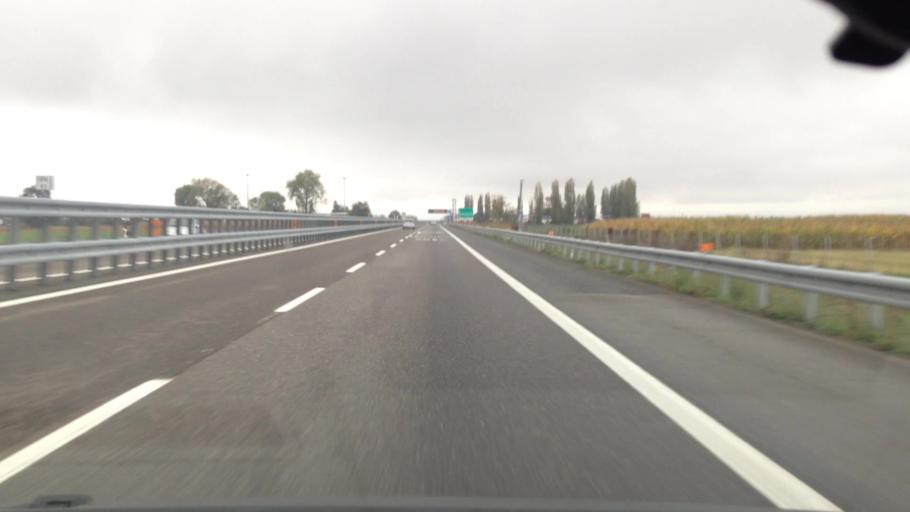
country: IT
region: Piedmont
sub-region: Provincia di Asti
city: San Paolo Solbrito
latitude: 44.9491
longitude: 7.9593
